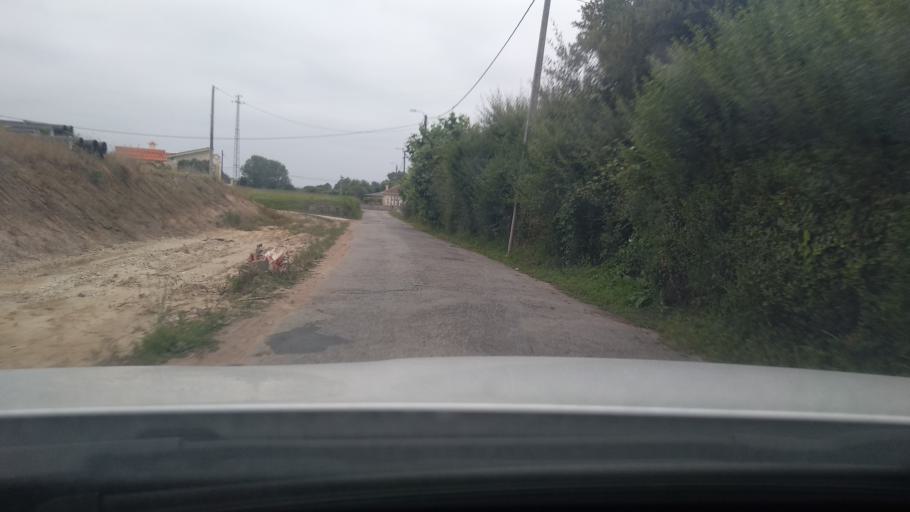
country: PT
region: Aveiro
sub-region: Espinho
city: Silvalde
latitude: 40.9880
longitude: -8.6347
